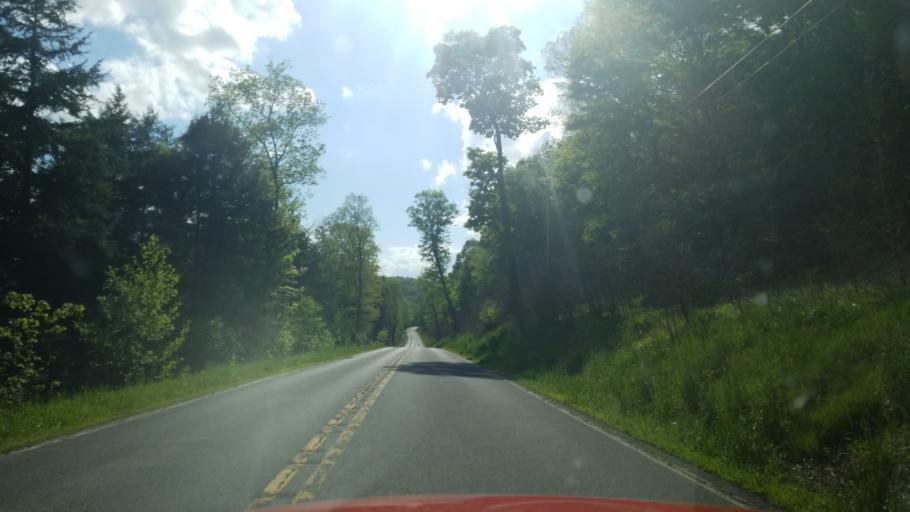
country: US
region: Pennsylvania
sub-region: Clearfield County
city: Hyde
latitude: 40.9708
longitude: -78.4162
